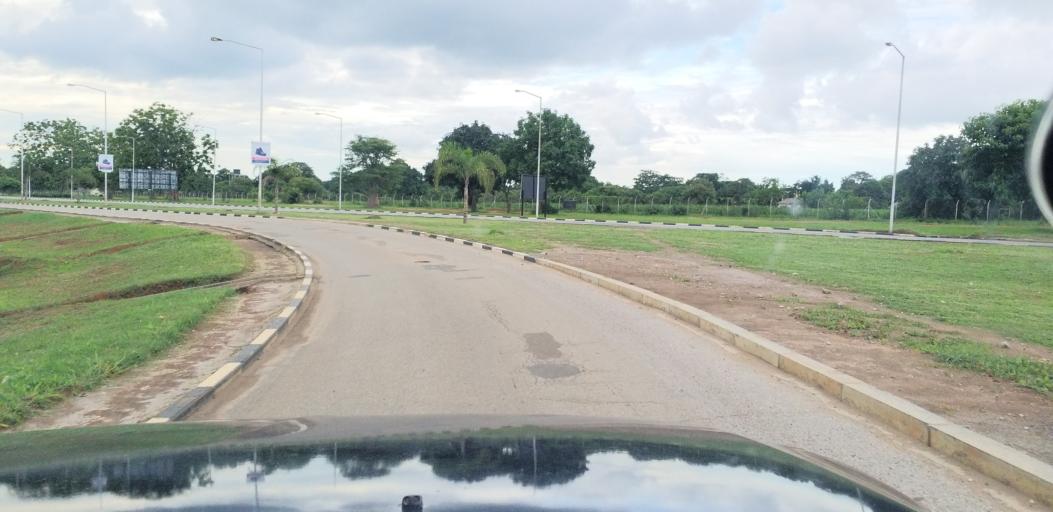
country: ZM
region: Lusaka
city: Lusaka
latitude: -15.3208
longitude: 28.4455
